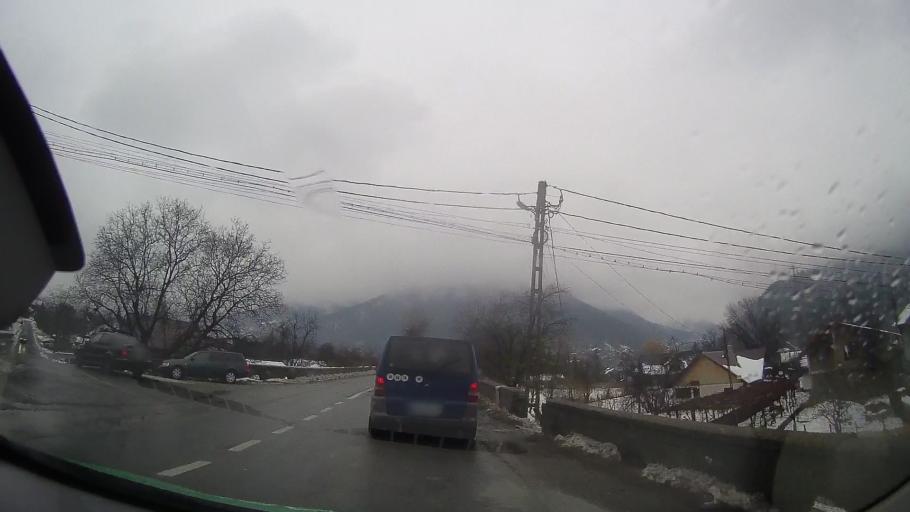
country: RO
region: Neamt
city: Viisoara
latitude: 46.9288
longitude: 26.2252
